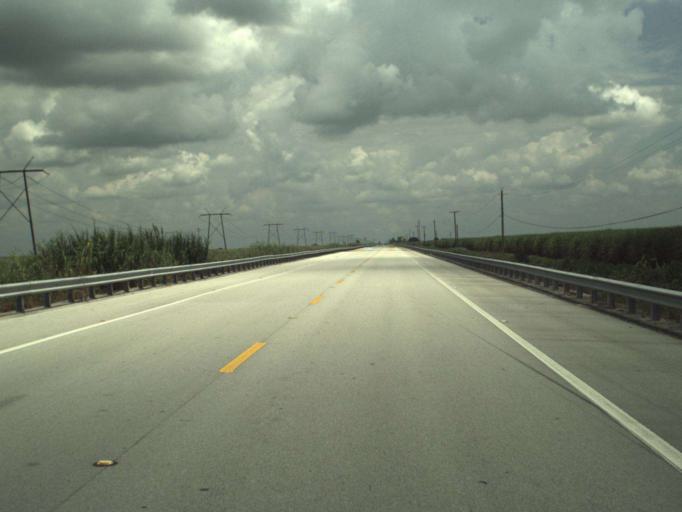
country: US
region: Florida
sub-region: Palm Beach County
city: Pahokee
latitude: 26.7803
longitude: -80.5207
